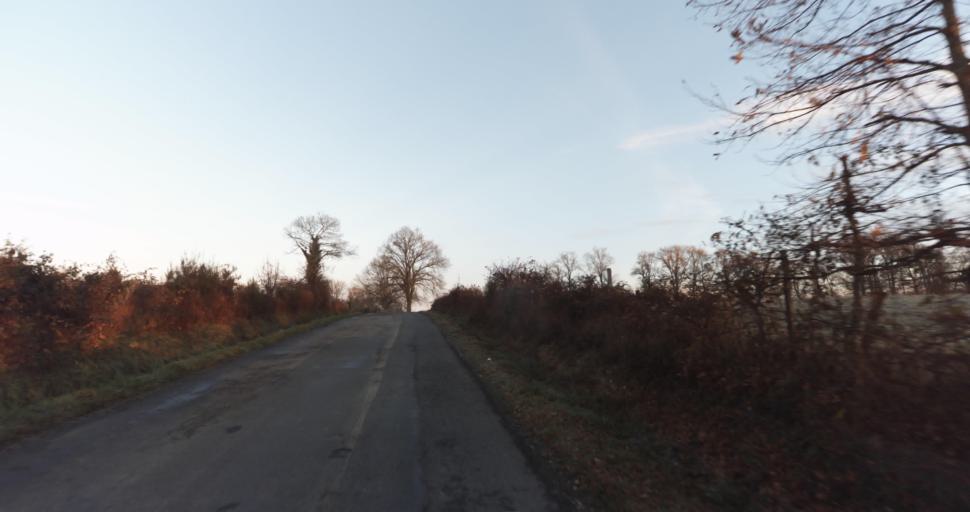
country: FR
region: Limousin
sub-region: Departement de la Haute-Vienne
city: Aixe-sur-Vienne
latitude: 45.8144
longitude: 1.1661
